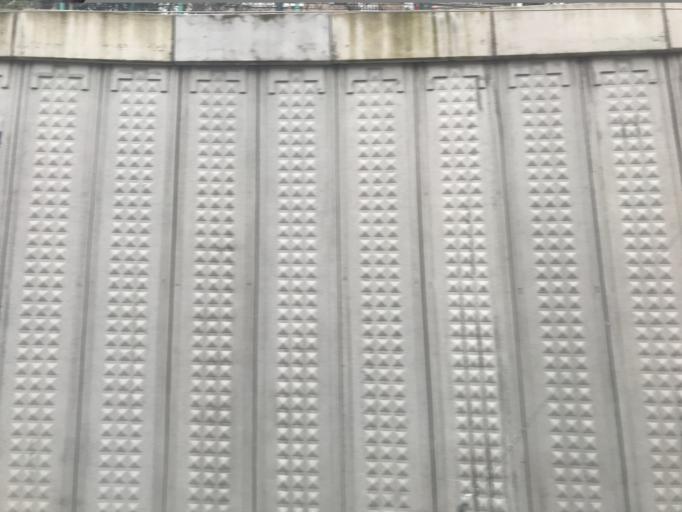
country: TR
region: Istanbul
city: Bahcelievler
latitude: 40.9797
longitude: 28.8694
